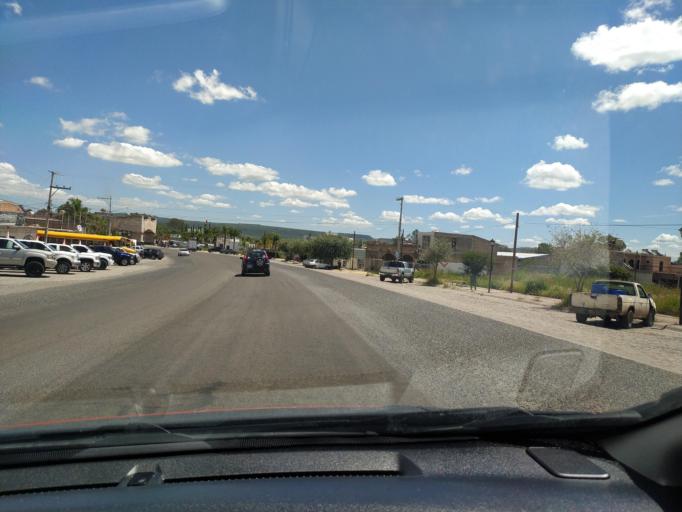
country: MX
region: Jalisco
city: San Diego de Alejandria
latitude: 20.9971
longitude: -101.9949
